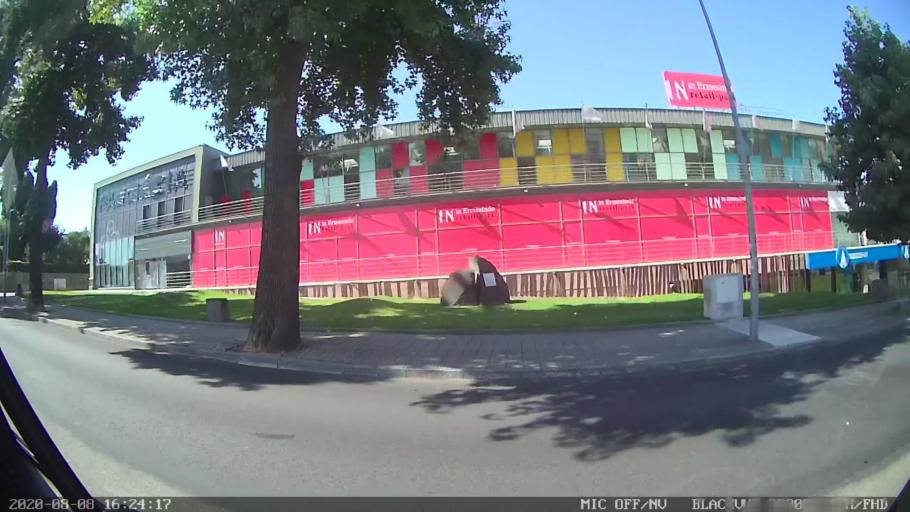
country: PT
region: Porto
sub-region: Gondomar
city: Baguim do Monte
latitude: 41.2047
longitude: -8.5509
